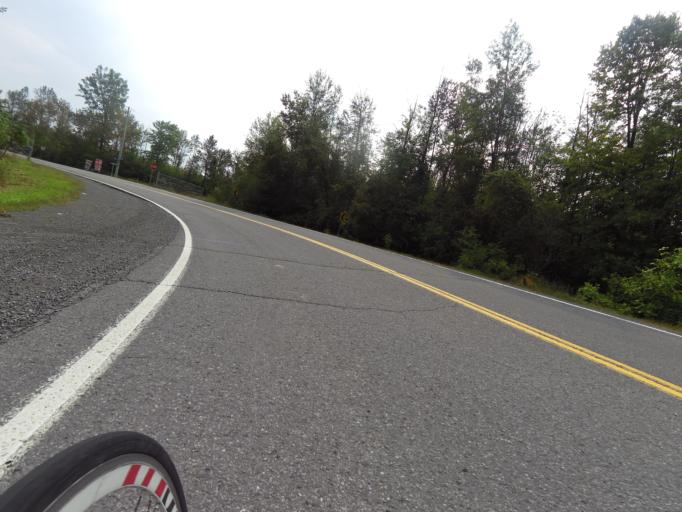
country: CA
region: Ontario
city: Bells Corners
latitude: 45.2258
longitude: -75.7523
